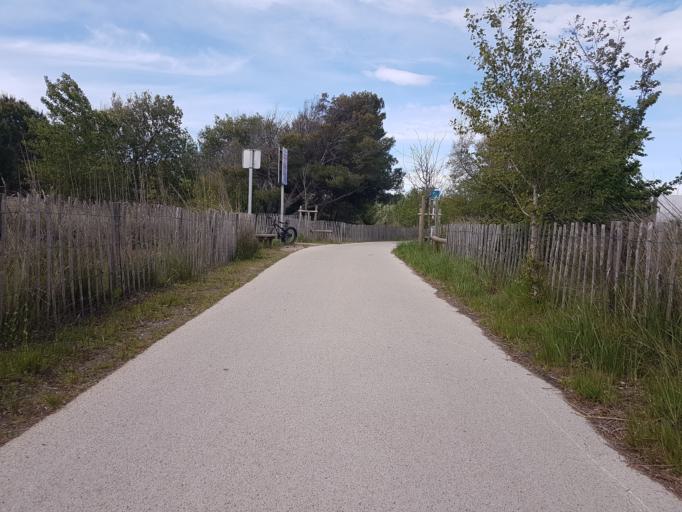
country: FR
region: Languedoc-Roussillon
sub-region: Departement de l'Herault
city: La Grande-Motte
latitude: 43.5579
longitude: 4.0249
